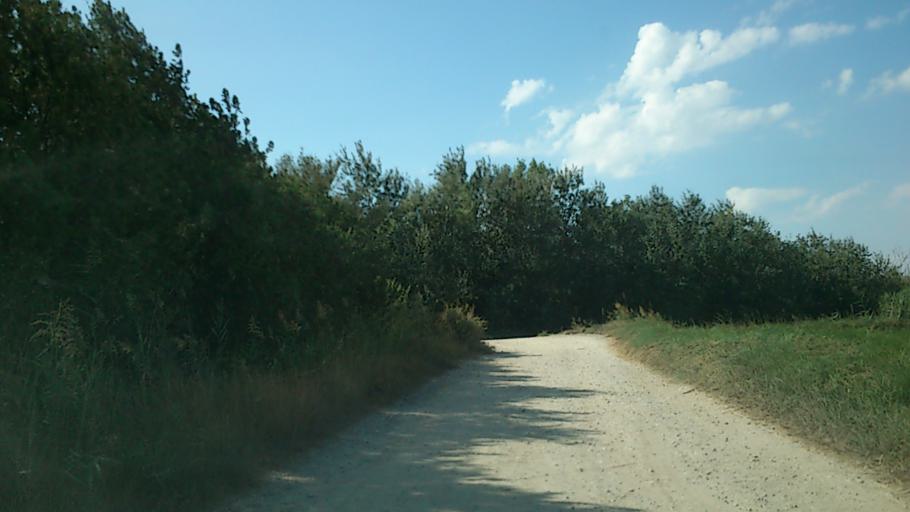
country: ES
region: Aragon
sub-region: Provincia de Zaragoza
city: Puebla de Alfinden
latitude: 41.6073
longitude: -0.7596
